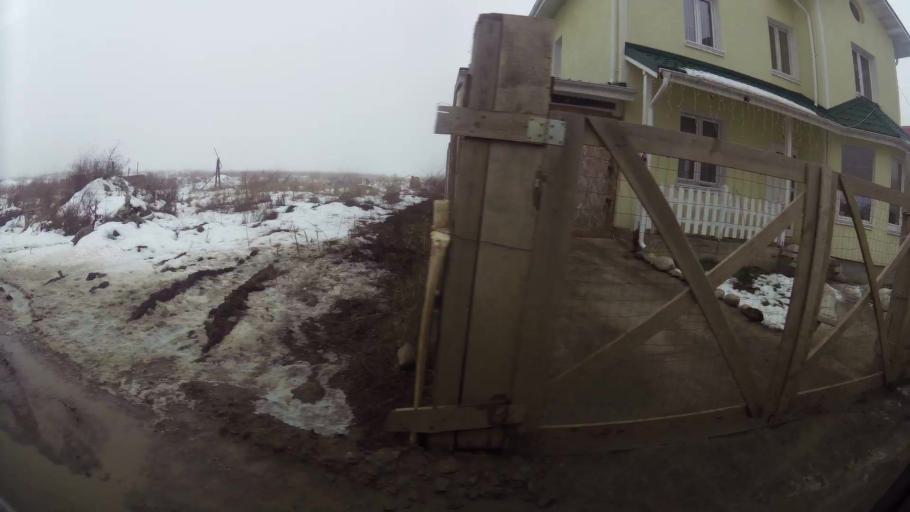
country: RO
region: Ilfov
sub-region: Comuna Chiajna
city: Chiajna
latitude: 44.4478
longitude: 25.9758
